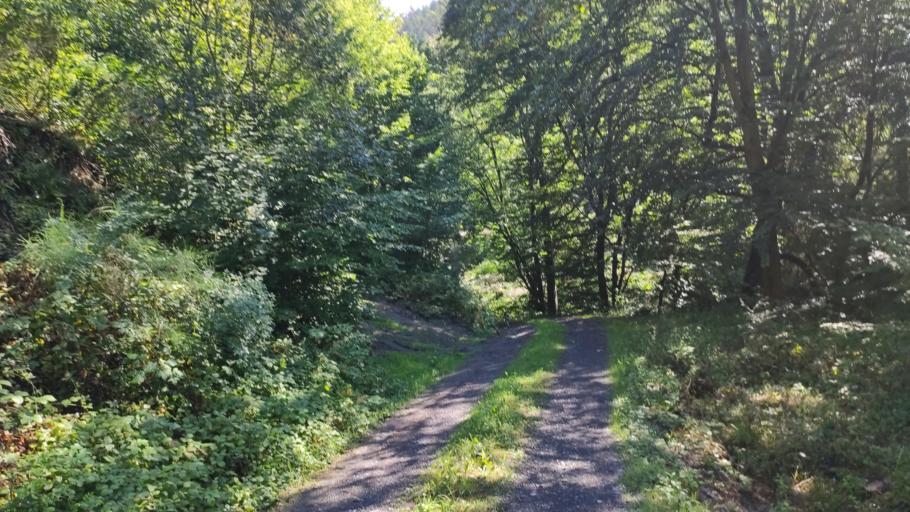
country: DE
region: Thuringia
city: Leutenberg
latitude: 50.5795
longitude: 11.4506
